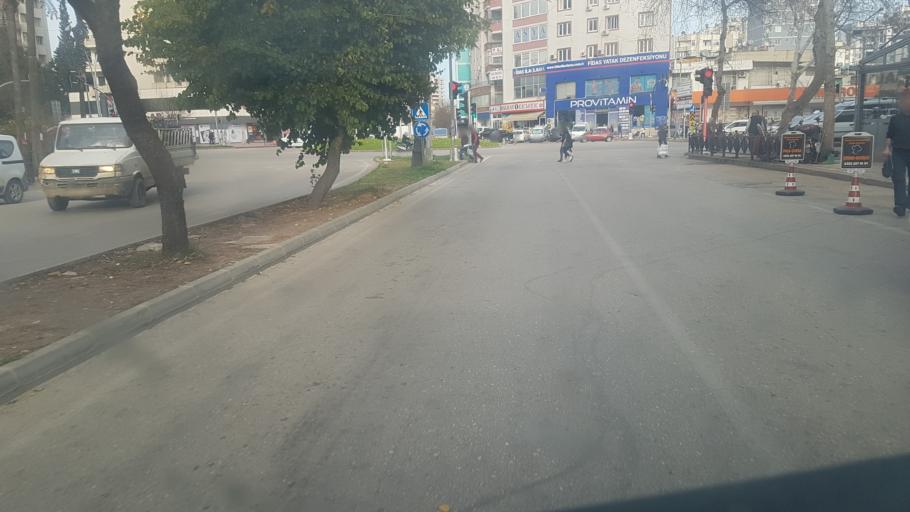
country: TR
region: Adana
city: Adana
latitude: 37.0271
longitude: 35.3131
